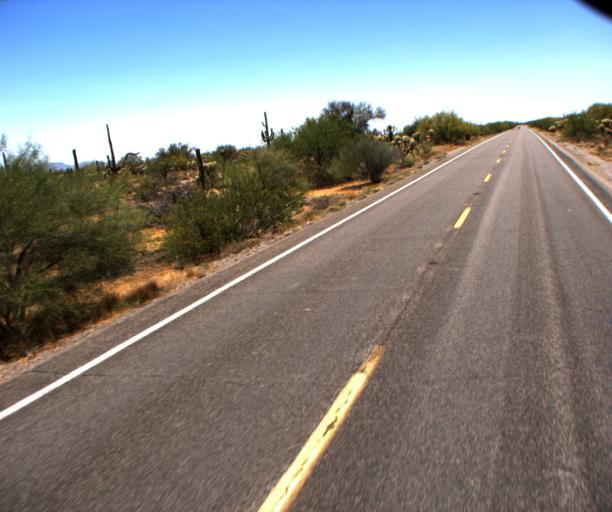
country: US
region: Arizona
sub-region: Pima County
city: Marana
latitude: 32.7555
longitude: -111.1398
